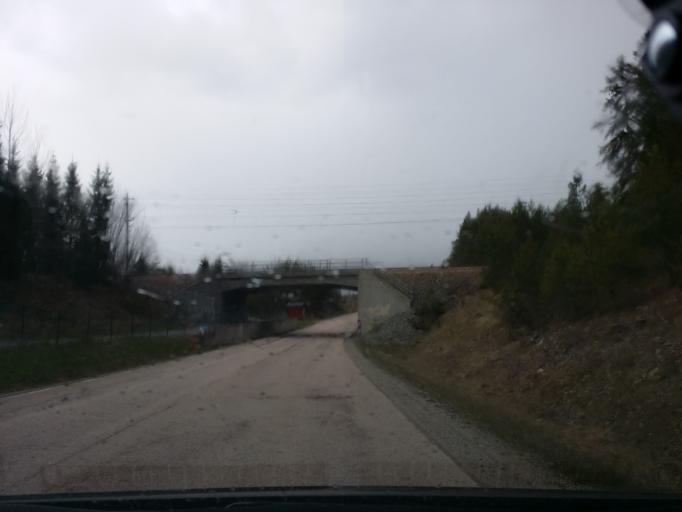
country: SE
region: Uppsala
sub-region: Enkopings Kommun
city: Enkoping
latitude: 59.6379
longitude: 17.1423
